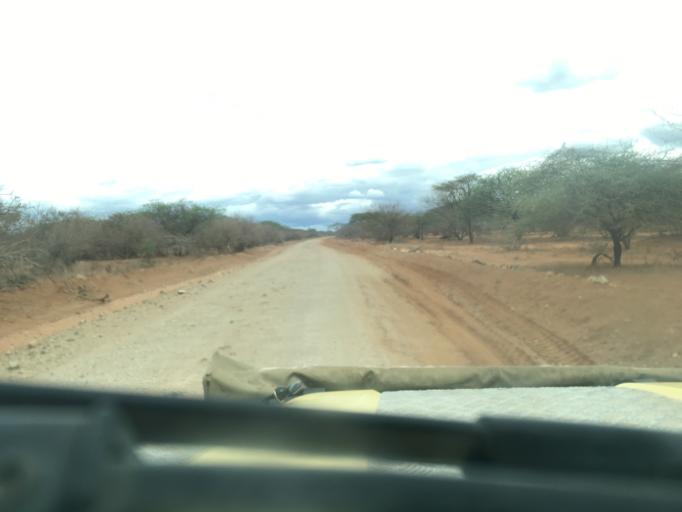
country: KE
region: Kajiado
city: Magadi
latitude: -2.2760
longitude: 35.7911
